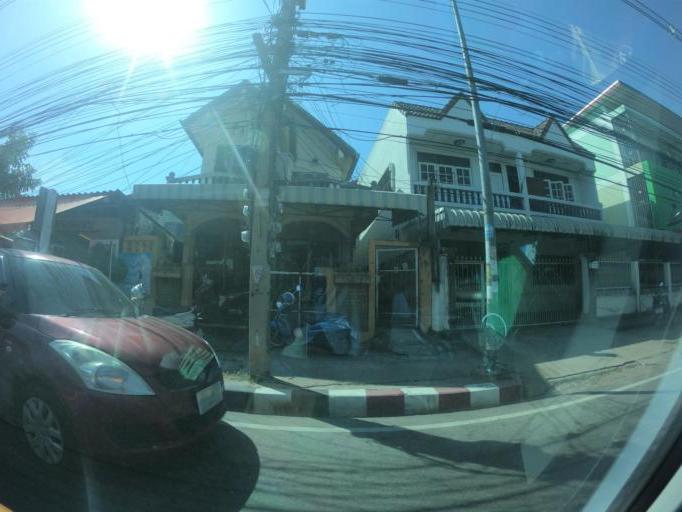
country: TH
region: Khon Kaen
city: Khon Kaen
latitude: 16.4110
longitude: 102.8337
